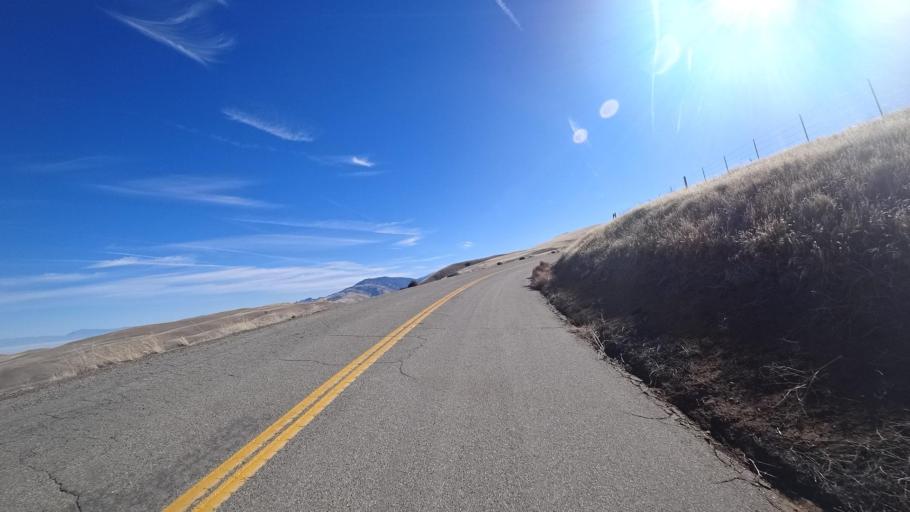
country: US
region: California
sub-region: Kern County
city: Maricopa
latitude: 34.9307
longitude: -119.4093
